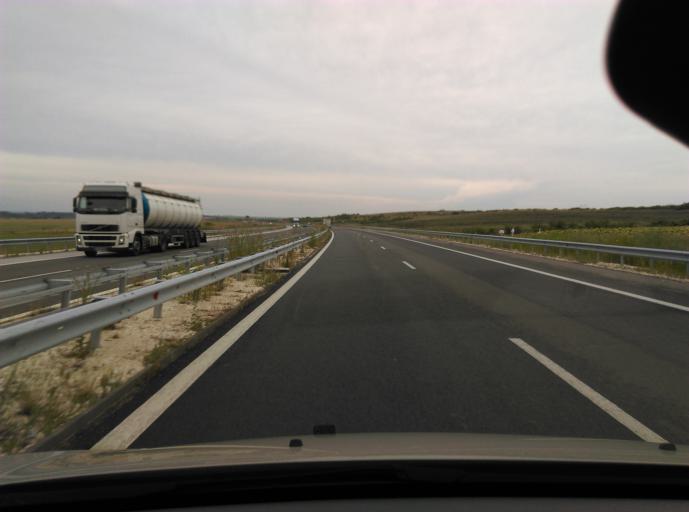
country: BG
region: Stara Zagora
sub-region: Obshtina Chirpan
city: Chirpan
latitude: 42.1174
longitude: 25.3995
